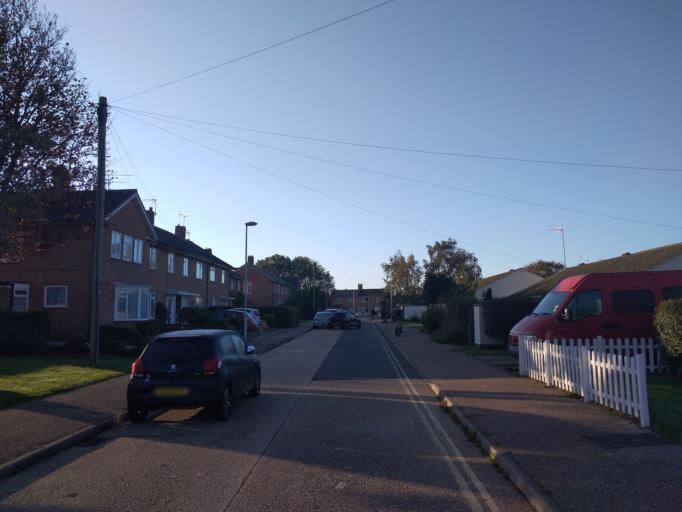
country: GB
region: England
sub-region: West Sussex
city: Goring-by-Sea
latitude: 50.8211
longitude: -0.4206
